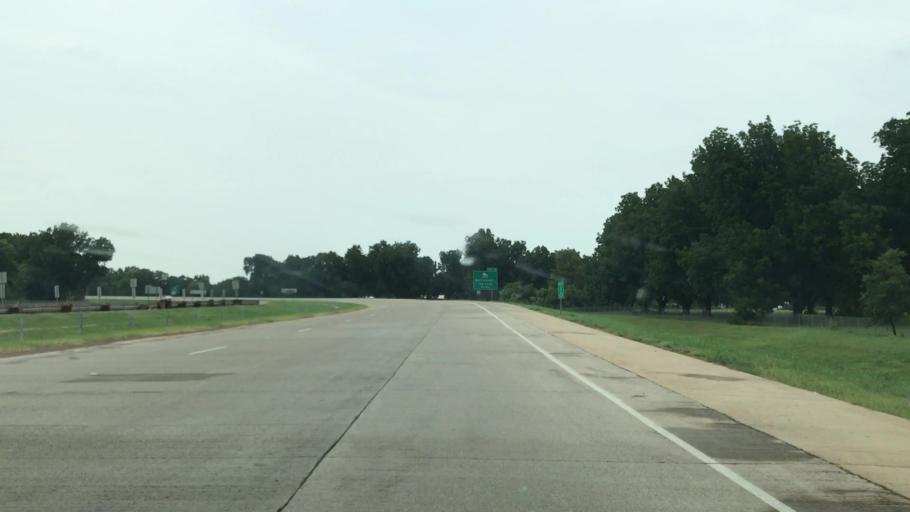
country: US
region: Louisiana
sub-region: Bossier Parish
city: Bossier City
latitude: 32.4039
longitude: -93.7144
